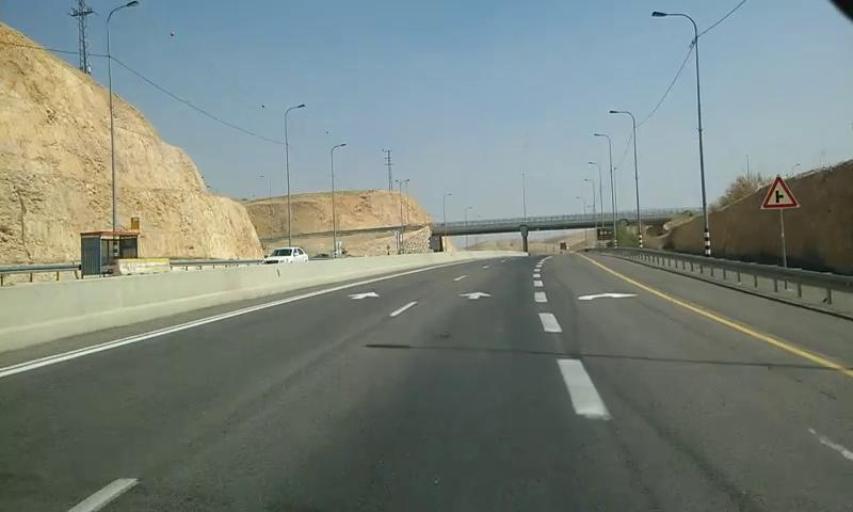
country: PS
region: West Bank
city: Hizma
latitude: 31.8170
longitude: 35.3619
